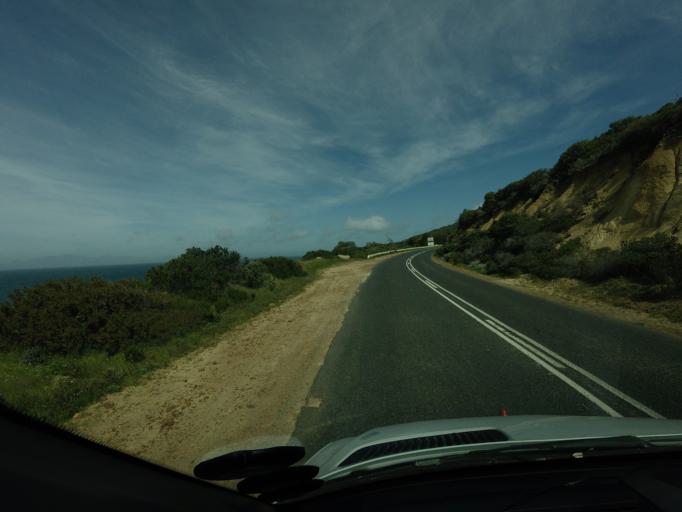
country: ZA
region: Western Cape
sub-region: City of Cape Town
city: Retreat
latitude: -34.2274
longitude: 18.4694
